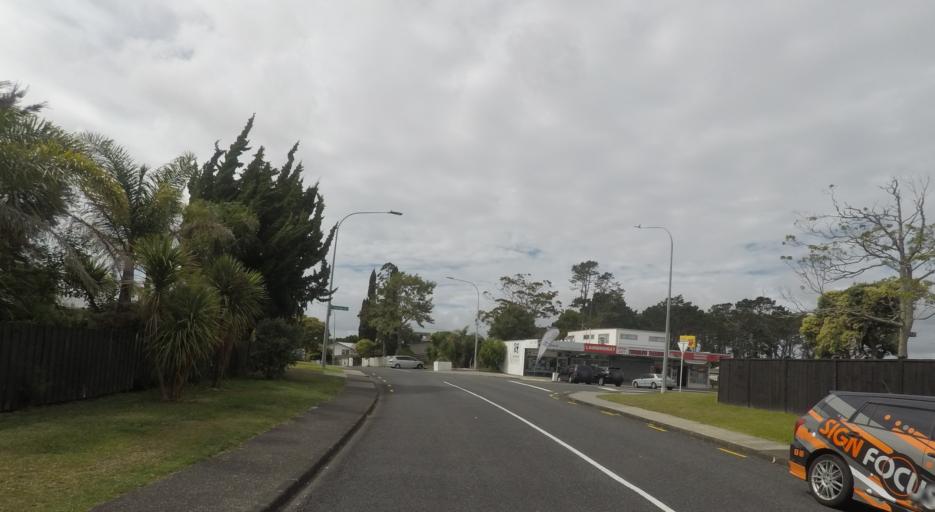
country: NZ
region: Auckland
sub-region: Auckland
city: Rosebank
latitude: -36.8894
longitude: 174.6489
